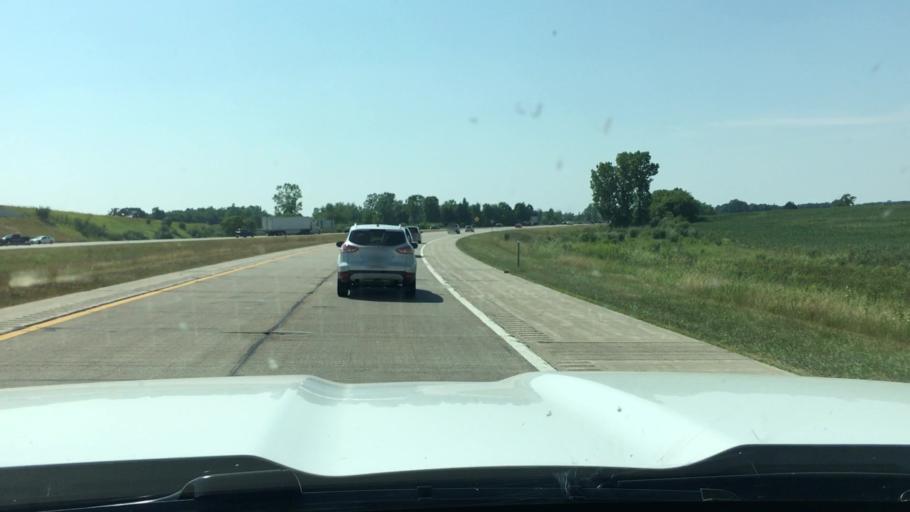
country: US
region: Michigan
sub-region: Clinton County
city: Wacousta
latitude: 42.7899
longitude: -84.6747
